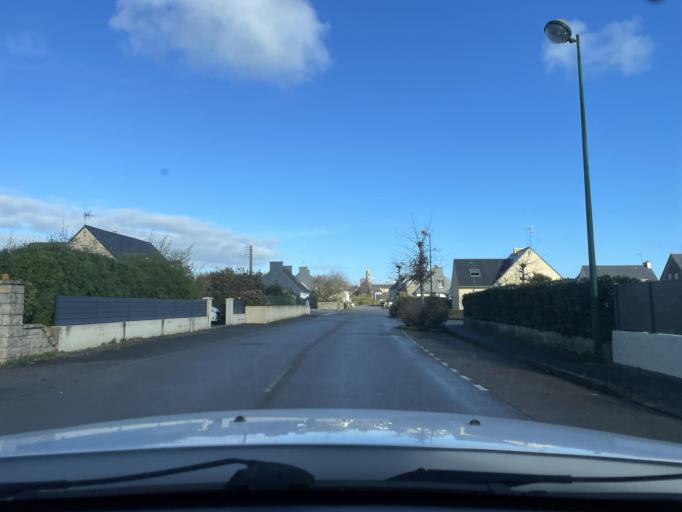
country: FR
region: Brittany
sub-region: Departement du Finistere
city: Edern
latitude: 48.1006
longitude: -3.9796
